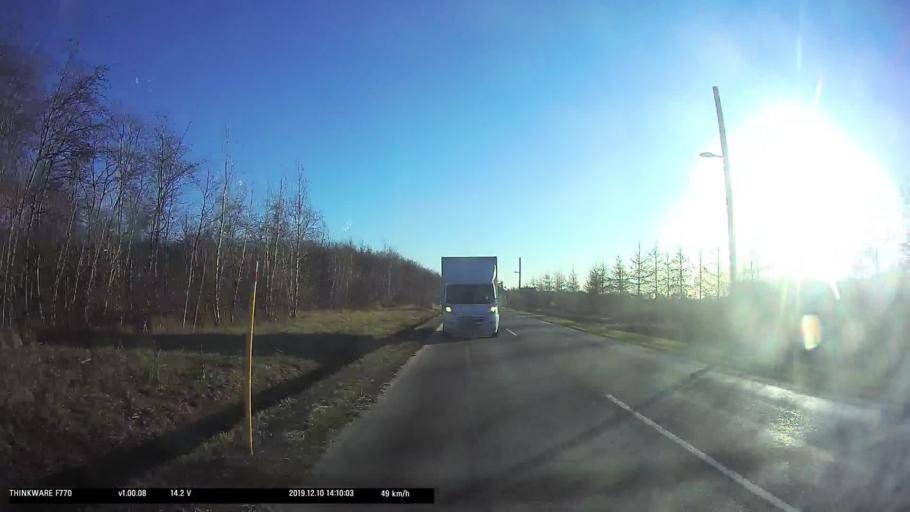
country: DK
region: Capital Region
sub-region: Tarnby Kommune
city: Tarnby
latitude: 55.5704
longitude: 12.5824
